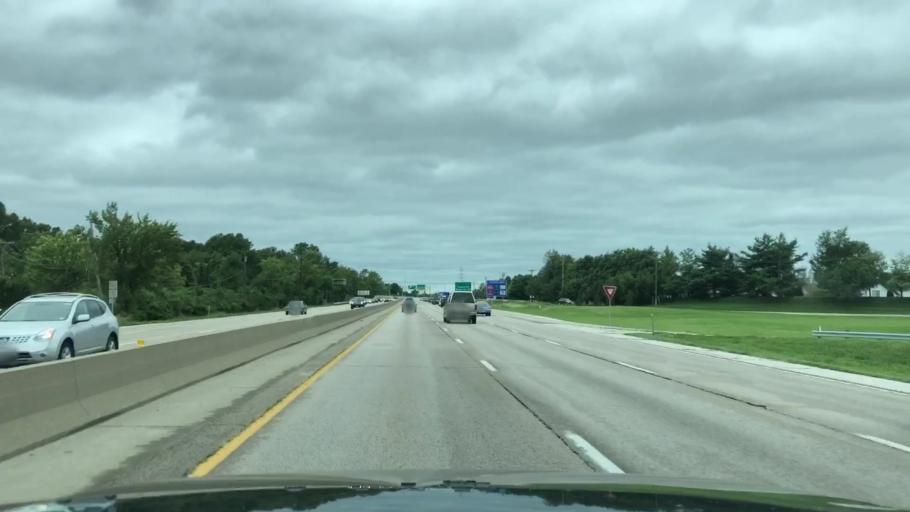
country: US
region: Missouri
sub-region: Saint Louis County
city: Manchester
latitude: 38.6346
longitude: -90.5132
